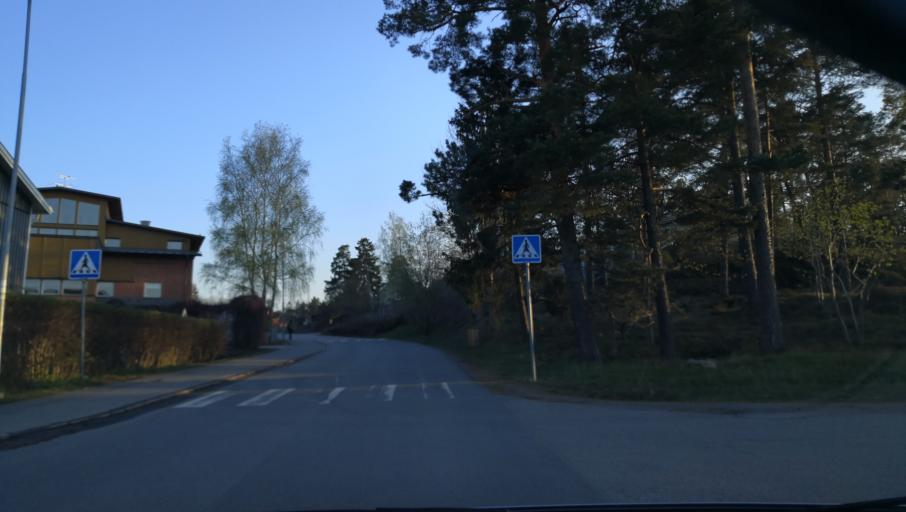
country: SE
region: Stockholm
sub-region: Varmdo Kommun
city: Mortnas
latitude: 59.3188
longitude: 18.4680
